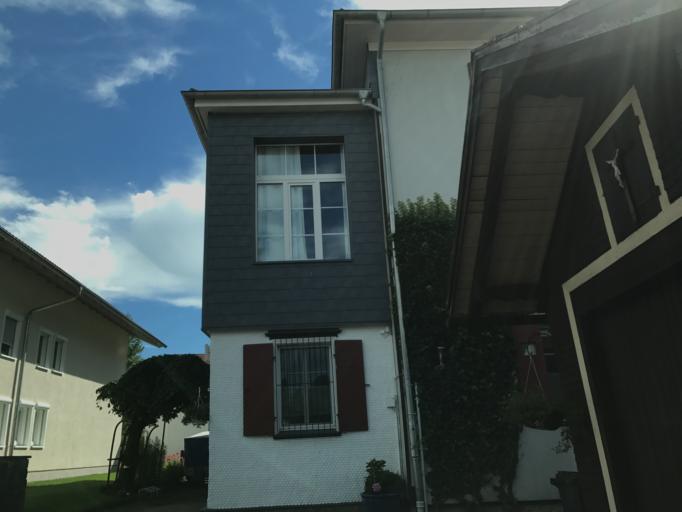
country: DE
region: Bavaria
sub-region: Swabia
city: Rothenbach
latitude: 47.6019
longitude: 9.9589
